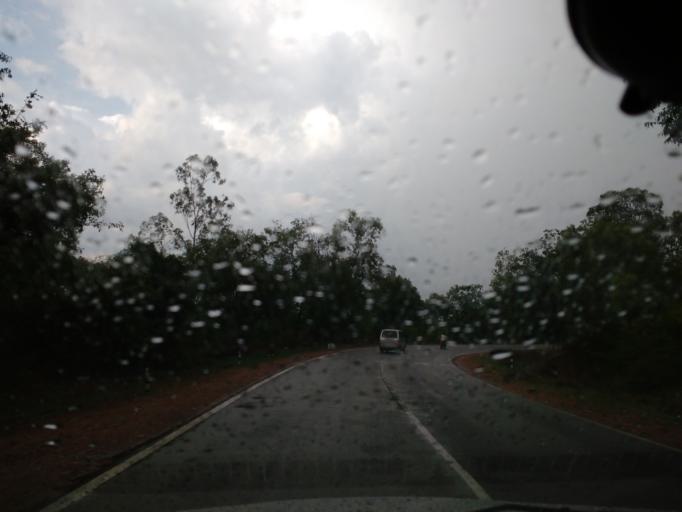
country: IN
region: Karnataka
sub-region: Tumkur
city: Chiknayakanhalli
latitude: 13.3042
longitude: 76.5929
